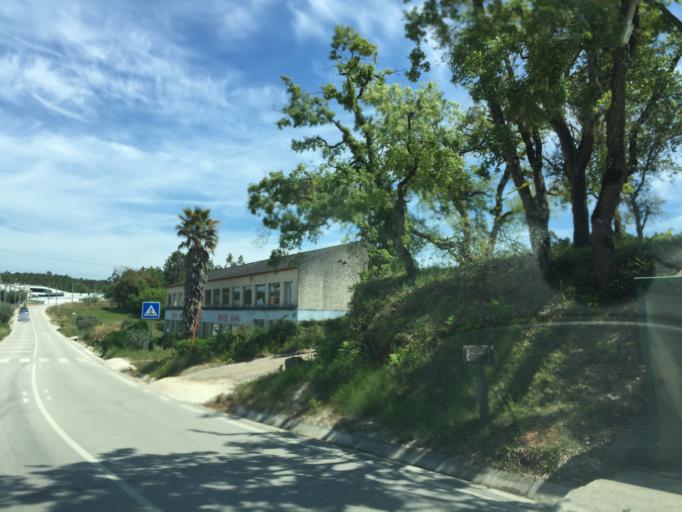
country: PT
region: Coimbra
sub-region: Soure
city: Soure
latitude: 40.0524
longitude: -8.6691
